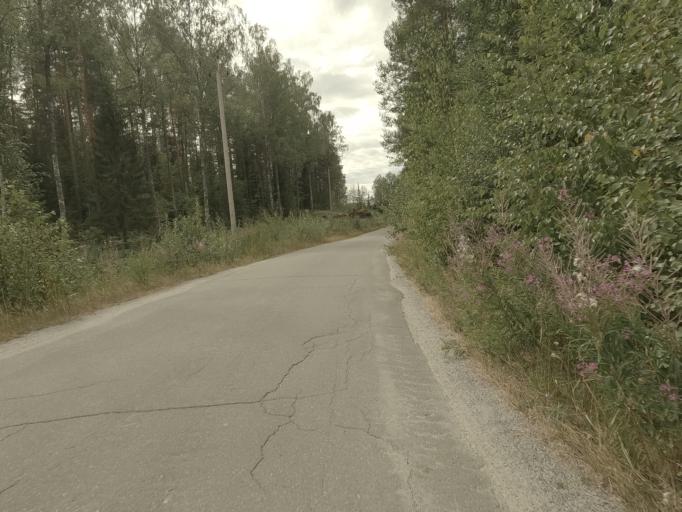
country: RU
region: Leningrad
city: Kamennogorsk
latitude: 60.9734
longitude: 29.1731
